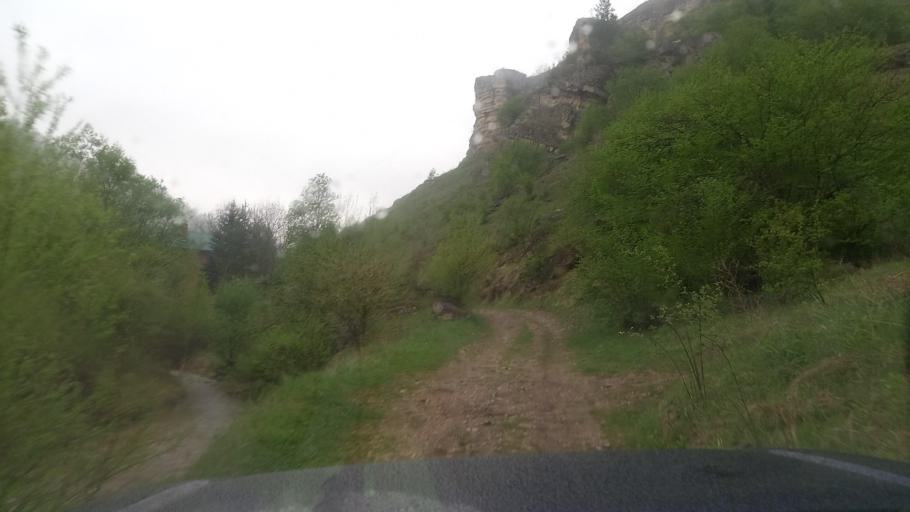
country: RU
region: Stavropol'skiy
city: Kislovodsk
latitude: 43.8824
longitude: 42.6955
